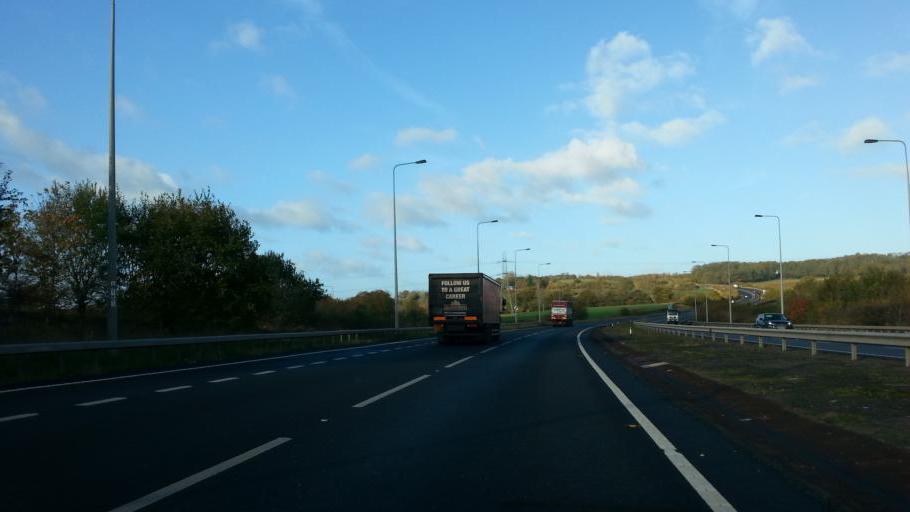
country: GB
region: England
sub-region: Staffordshire
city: Fazeley
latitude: 52.6235
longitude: -1.7431
